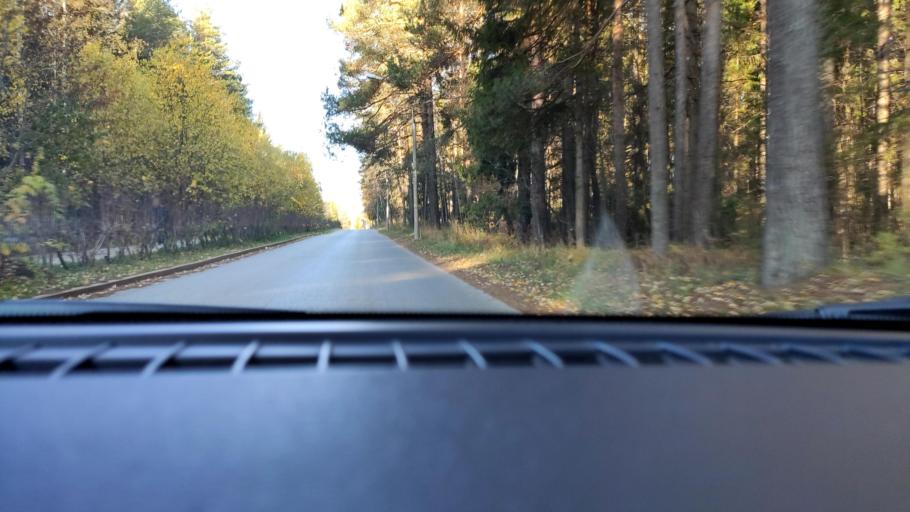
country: RU
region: Perm
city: Perm
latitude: 58.0555
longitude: 56.2210
